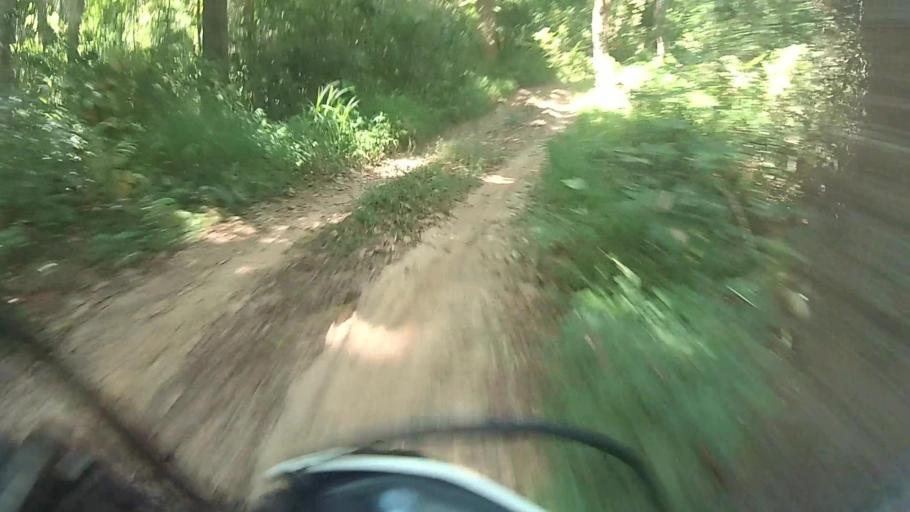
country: TH
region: Chiang Mai
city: Samoeng
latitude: 18.9274
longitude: 98.8604
